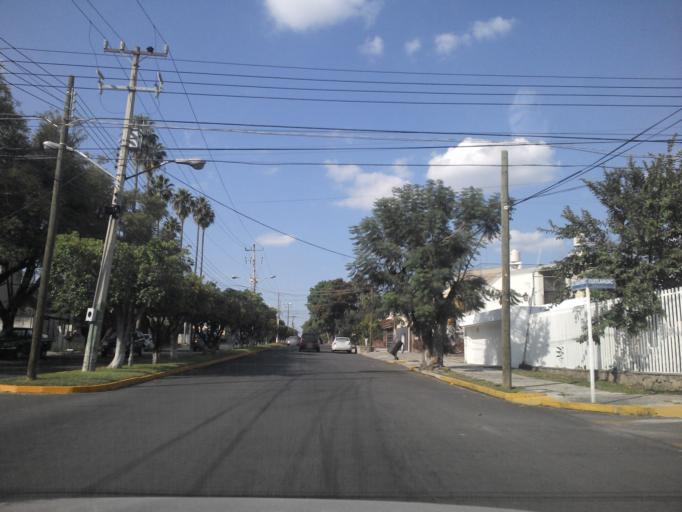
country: MX
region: Jalisco
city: Guadalajara
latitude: 20.6517
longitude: -103.4081
